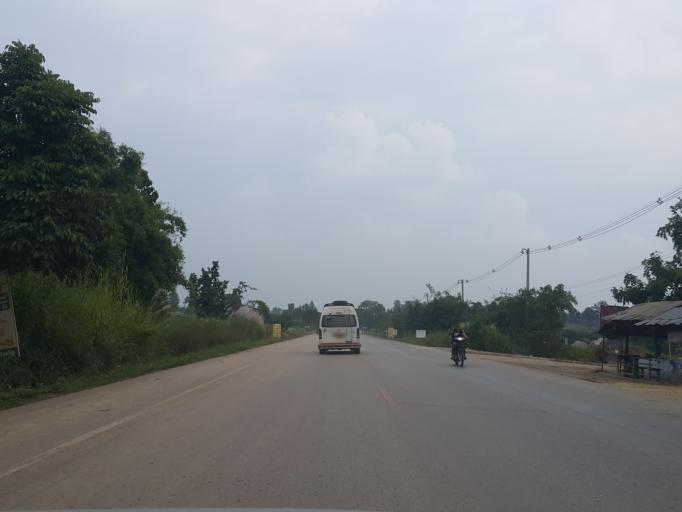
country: TH
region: Chiang Mai
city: Mae Taeng
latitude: 19.0854
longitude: 98.9083
